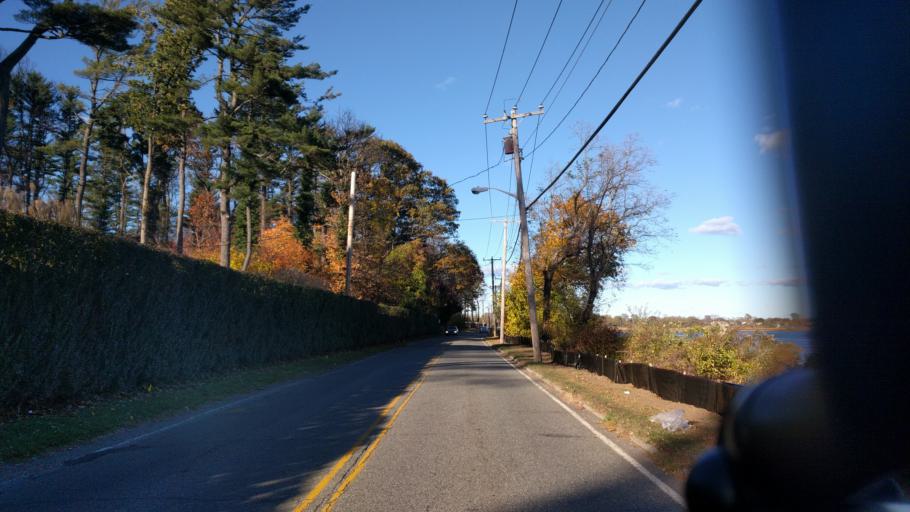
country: US
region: New York
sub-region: Nassau County
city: Bayville
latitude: 40.8973
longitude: -73.5492
